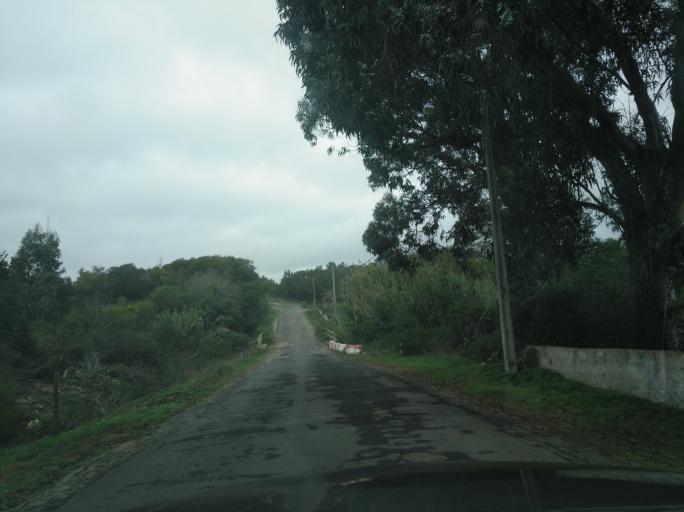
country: PT
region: Setubal
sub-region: Sines
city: Porto Covo
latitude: 37.8311
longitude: -8.7872
